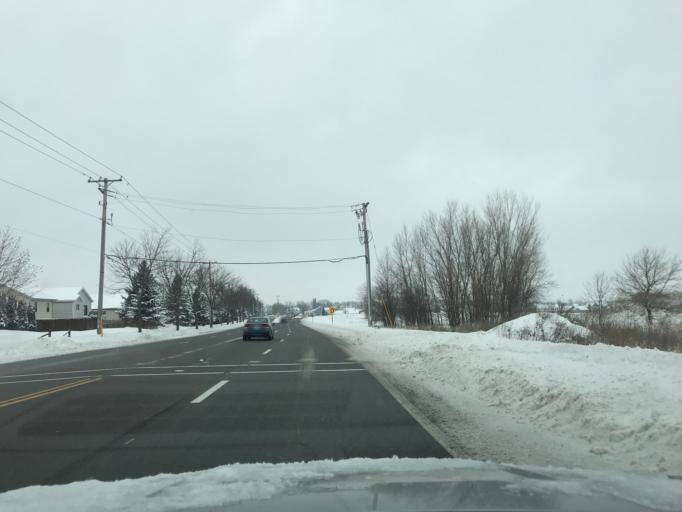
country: US
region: Wisconsin
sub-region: Dane County
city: Sun Prairie
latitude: 43.1615
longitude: -89.2850
